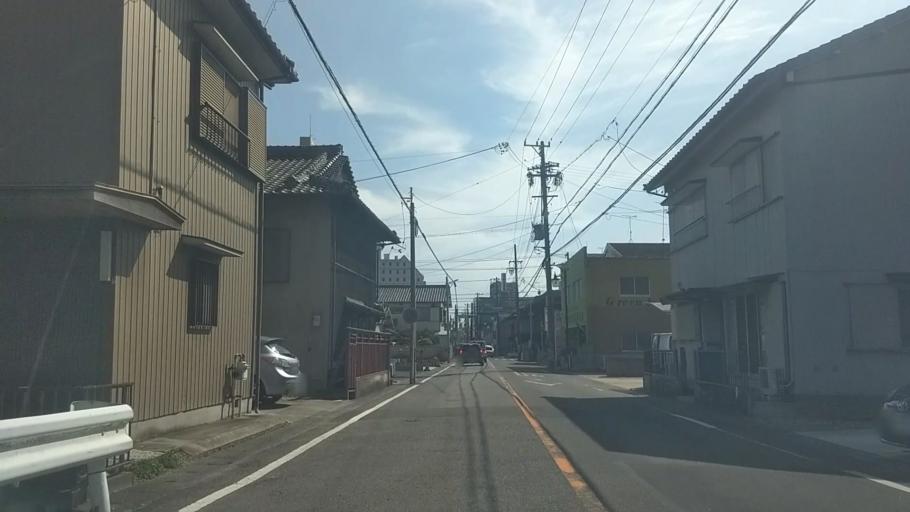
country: JP
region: Aichi
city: Anjo
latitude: 34.9619
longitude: 137.0905
